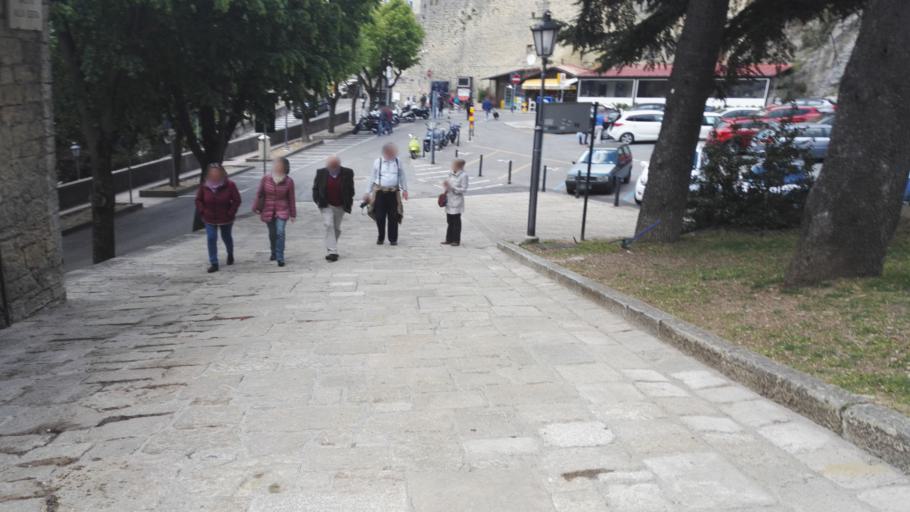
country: SM
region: San Marino
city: San Marino
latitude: 43.9343
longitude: 12.4494
